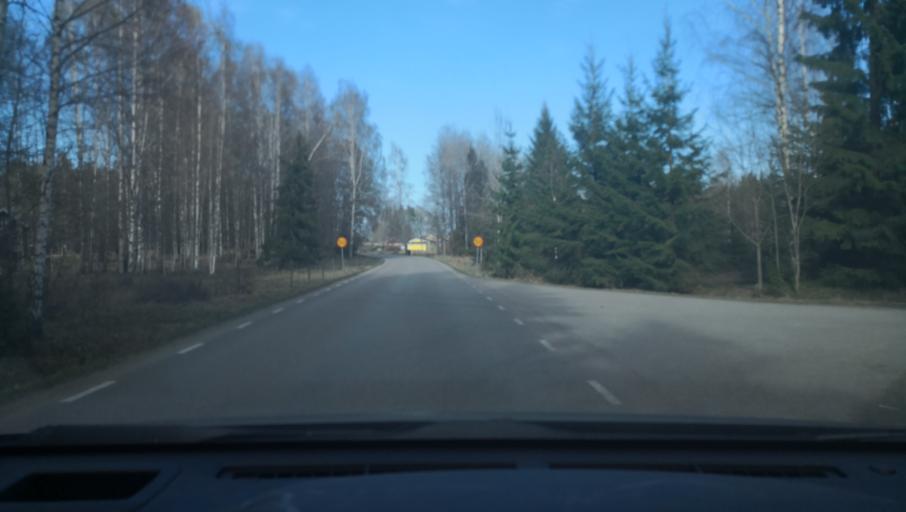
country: SE
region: Uppsala
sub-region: Heby Kommun
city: Heby
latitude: 59.9217
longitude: 16.8475
